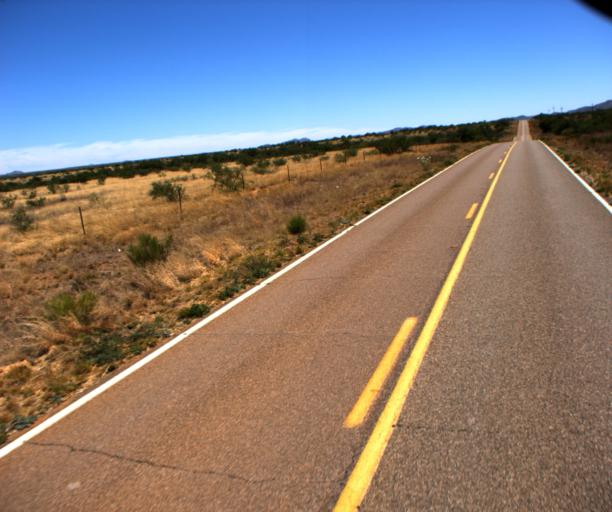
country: US
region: Arizona
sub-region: Pima County
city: Arivaca Junction
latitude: 31.6173
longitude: -111.5154
